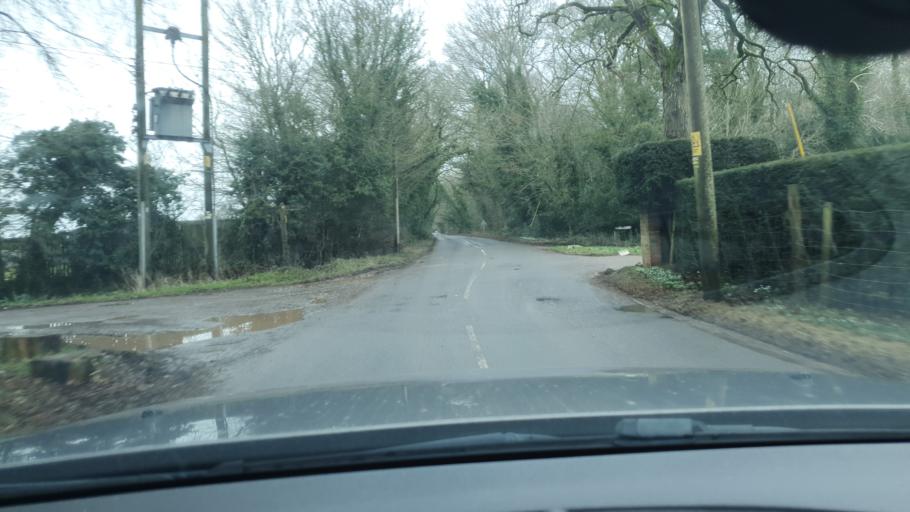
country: GB
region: England
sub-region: West Berkshire
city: Greenham
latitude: 51.3535
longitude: -1.3223
